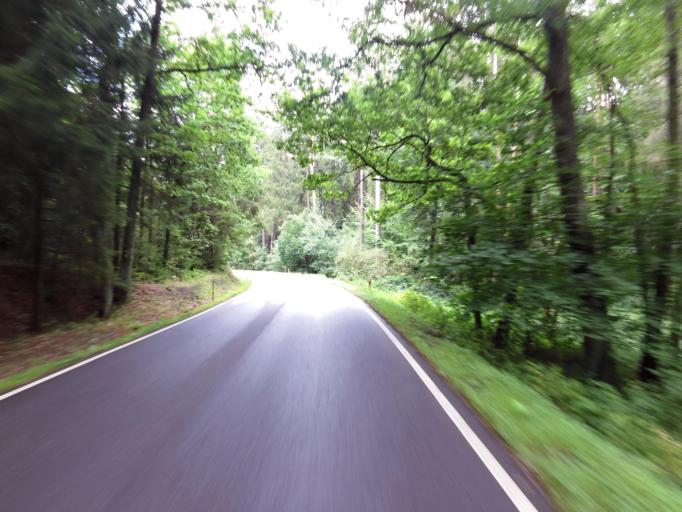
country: CZ
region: Jihocesky
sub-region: Okres Ceske Budejovice
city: Nove Hrady
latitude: 48.7768
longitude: 14.7674
